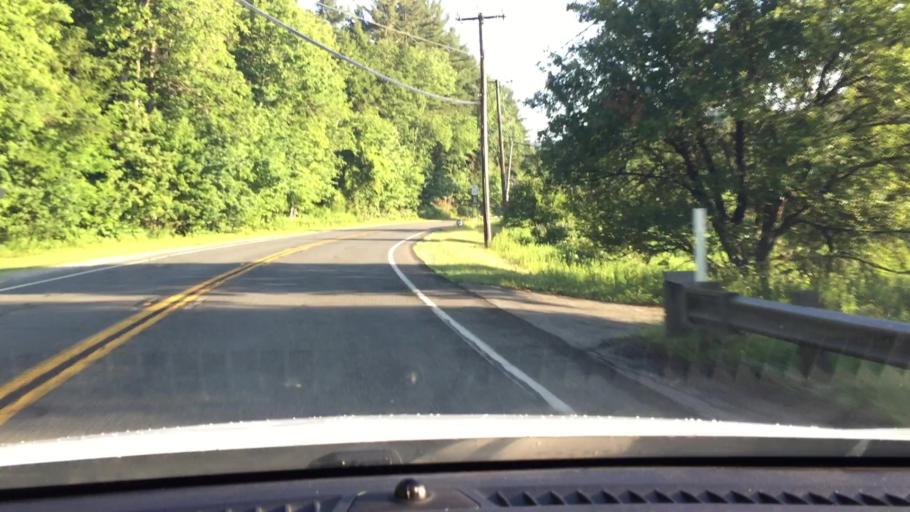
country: US
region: Massachusetts
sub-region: Berkshire County
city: Becket
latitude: 42.2657
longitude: -73.1362
